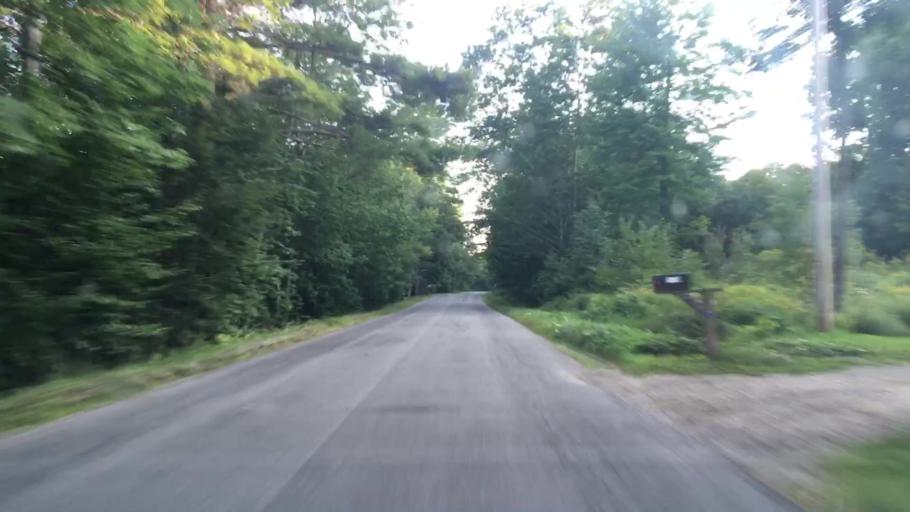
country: US
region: Maine
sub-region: Waldo County
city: Frankfort
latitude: 44.6648
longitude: -68.9267
